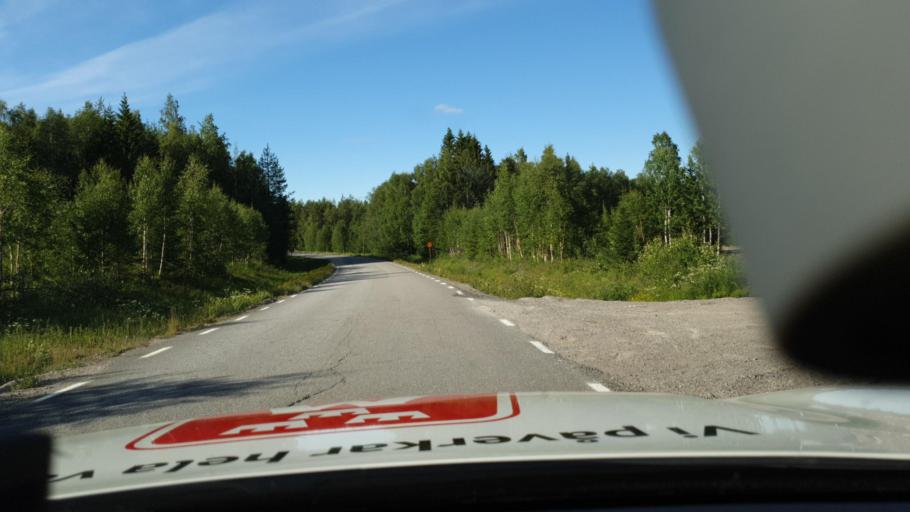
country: SE
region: Norrbotten
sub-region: Kalix Kommun
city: Toere
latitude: 65.8502
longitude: 22.6793
